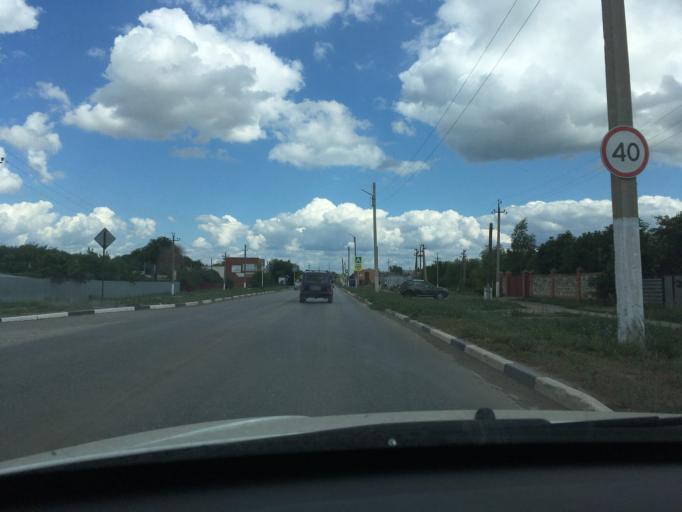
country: RU
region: Samara
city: Bezenchuk
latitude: 52.9901
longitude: 49.4360
